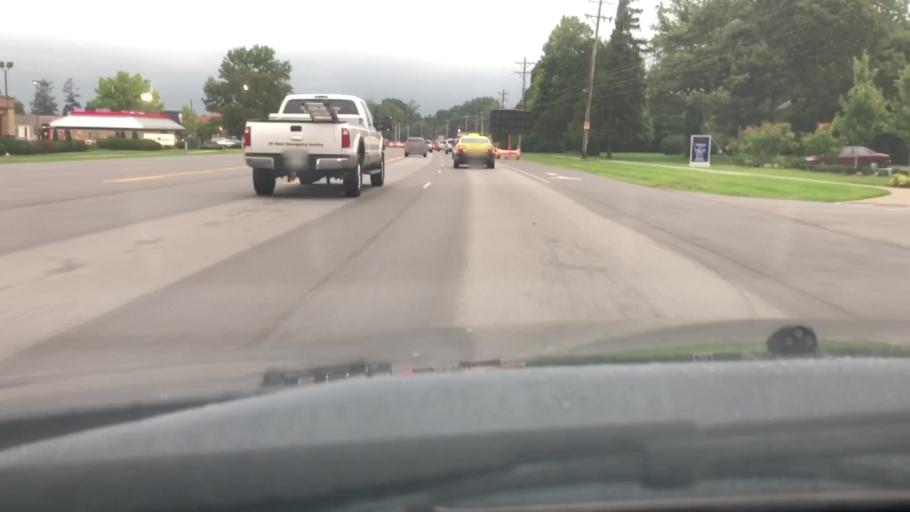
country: US
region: Kentucky
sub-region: Jefferson County
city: Hurstbourne Acres
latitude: 38.2132
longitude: -85.5881
